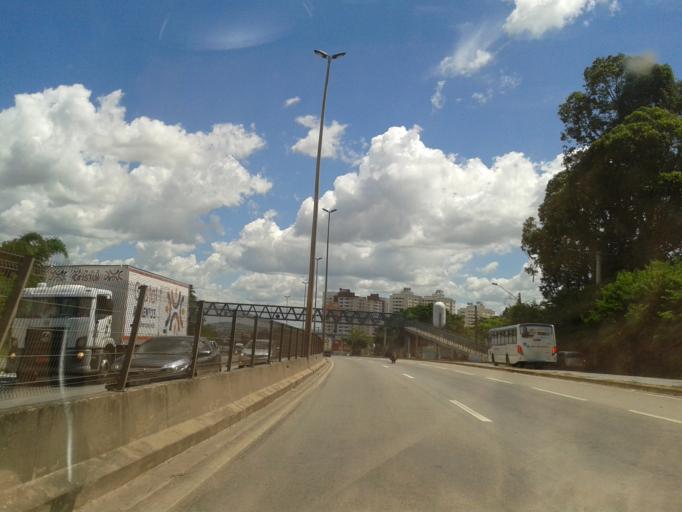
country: BR
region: Goias
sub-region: Goiania
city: Goiania
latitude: -16.7318
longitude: -49.2436
